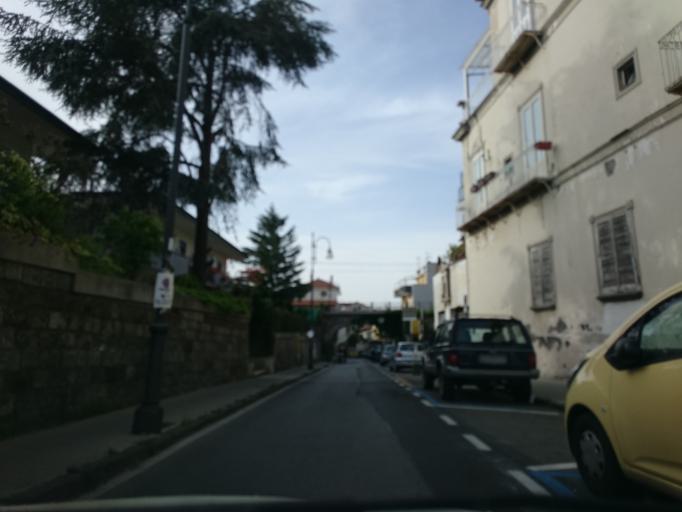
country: IT
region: Campania
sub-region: Provincia di Napoli
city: Sant'Agnello
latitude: 40.6315
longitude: 14.4019
